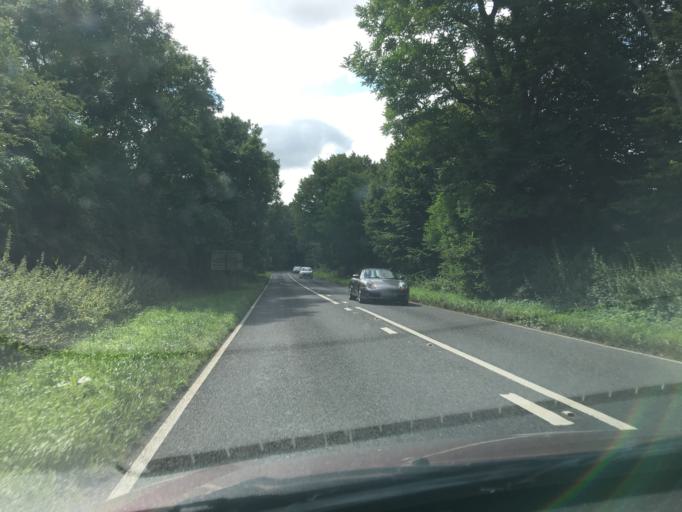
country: GB
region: England
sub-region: Warwickshire
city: Royal Leamington Spa
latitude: 52.3414
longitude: -1.5166
